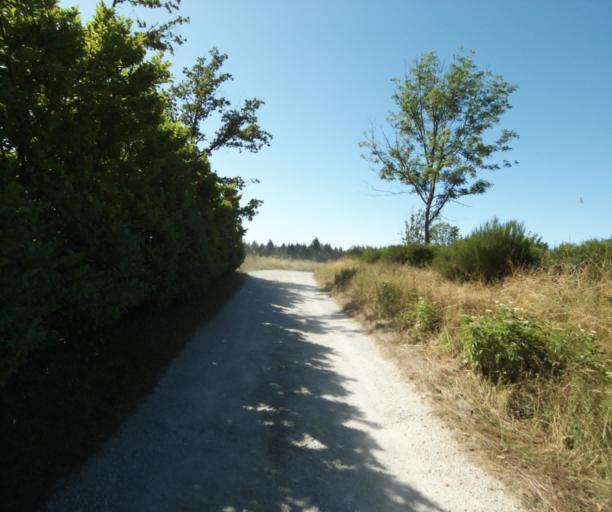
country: FR
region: Midi-Pyrenees
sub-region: Departement du Tarn
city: Soreze
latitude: 43.4240
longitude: 2.1217
